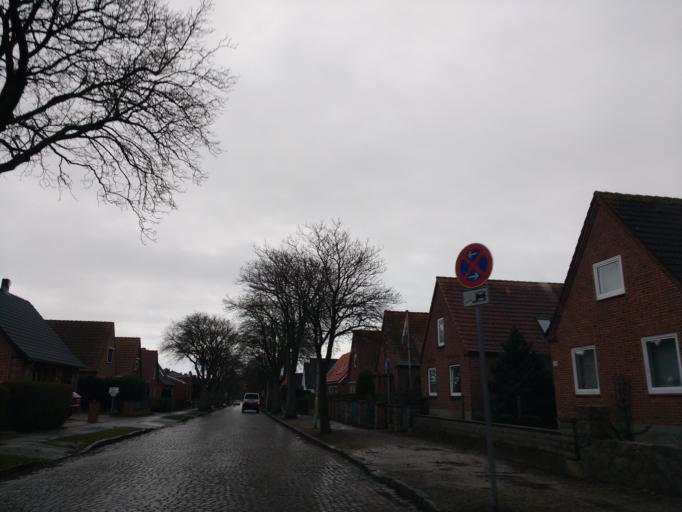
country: DE
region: Schleswig-Holstein
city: Burg auf Fehmarn
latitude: 54.4285
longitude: 11.1940
